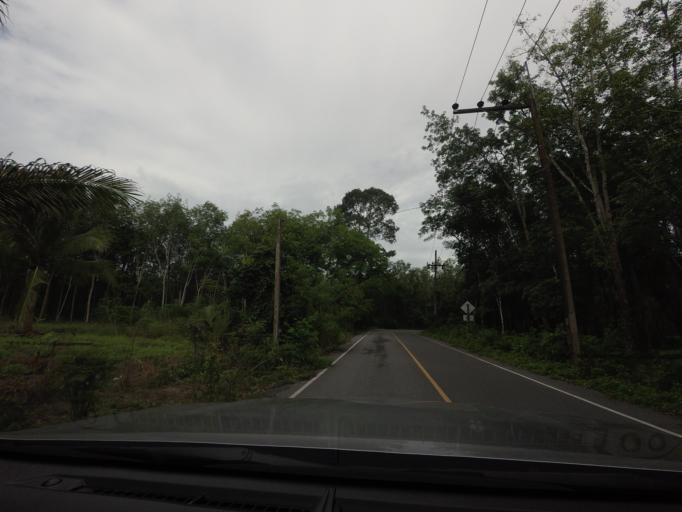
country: TH
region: Nakhon Si Thammarat
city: Phra Phrom
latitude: 8.2797
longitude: 99.9411
